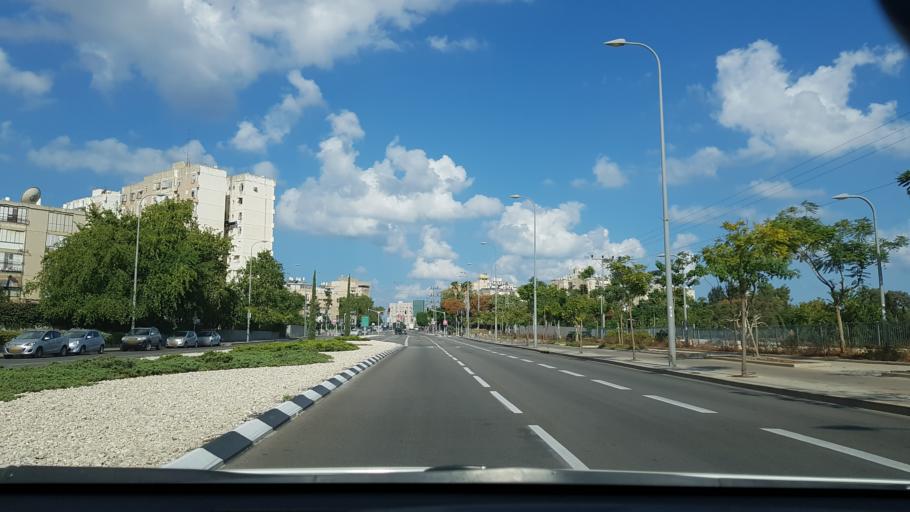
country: IL
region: Tel Aviv
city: Holon
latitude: 32.0091
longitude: 34.7962
